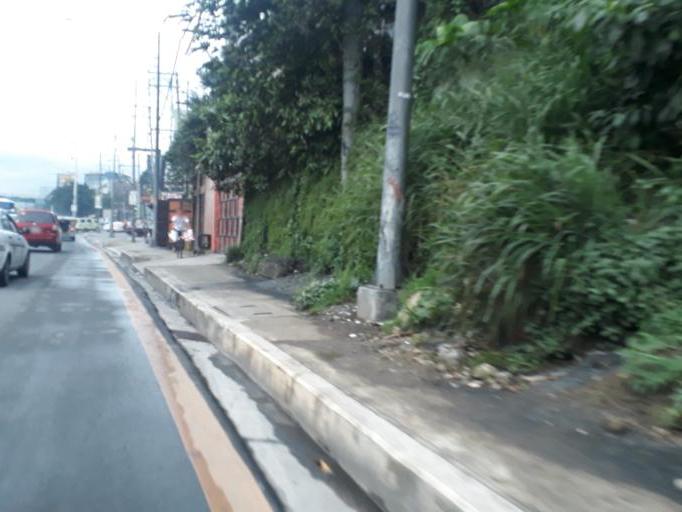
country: PH
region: Metro Manila
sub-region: Quezon City
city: Quezon City
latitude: 14.6725
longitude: 121.0800
